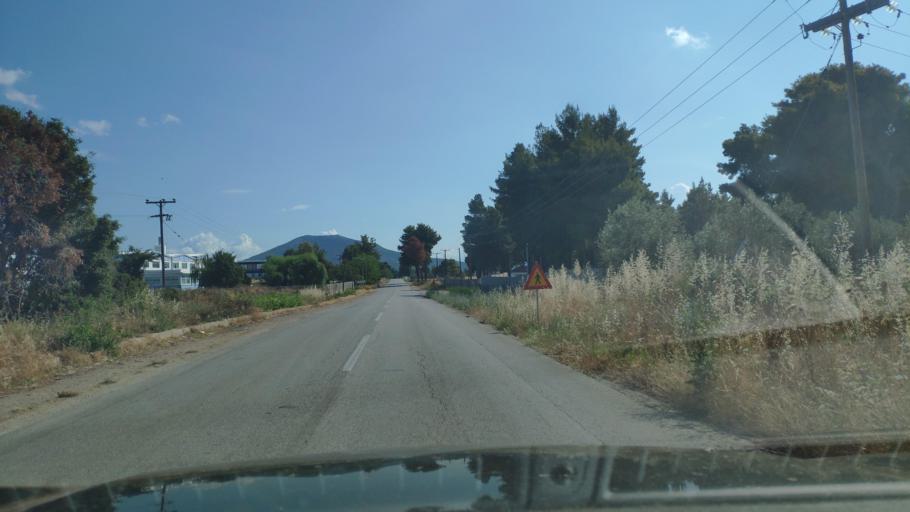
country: GR
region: Central Greece
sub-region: Nomos Voiotias
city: Arma
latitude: 38.3874
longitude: 23.5023
